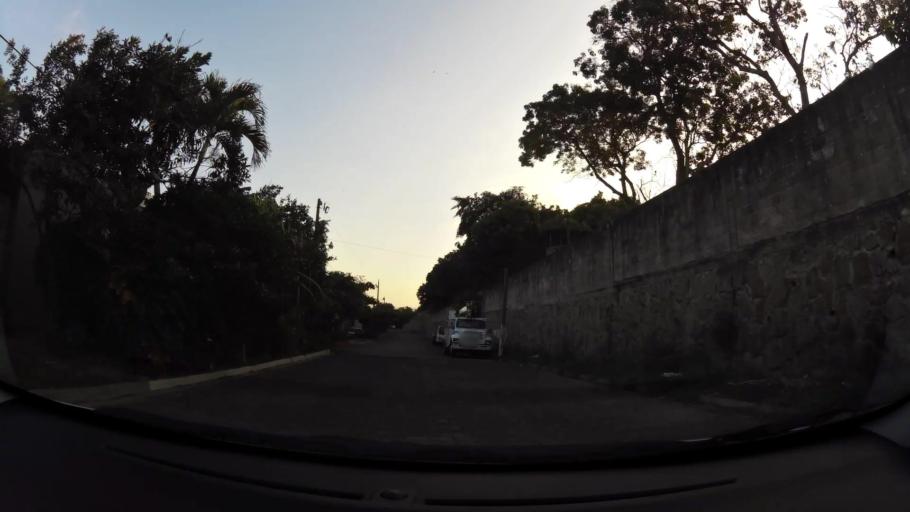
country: SV
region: San Salvador
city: Cuscatancingo
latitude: 13.7169
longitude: -89.1945
